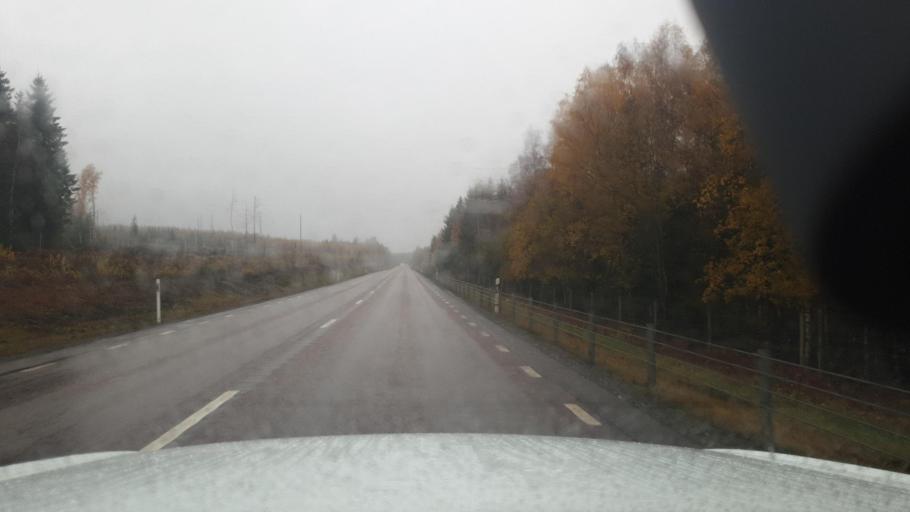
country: SE
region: Vaermland
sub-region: Sunne Kommun
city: Sunne
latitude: 59.7541
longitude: 13.1182
